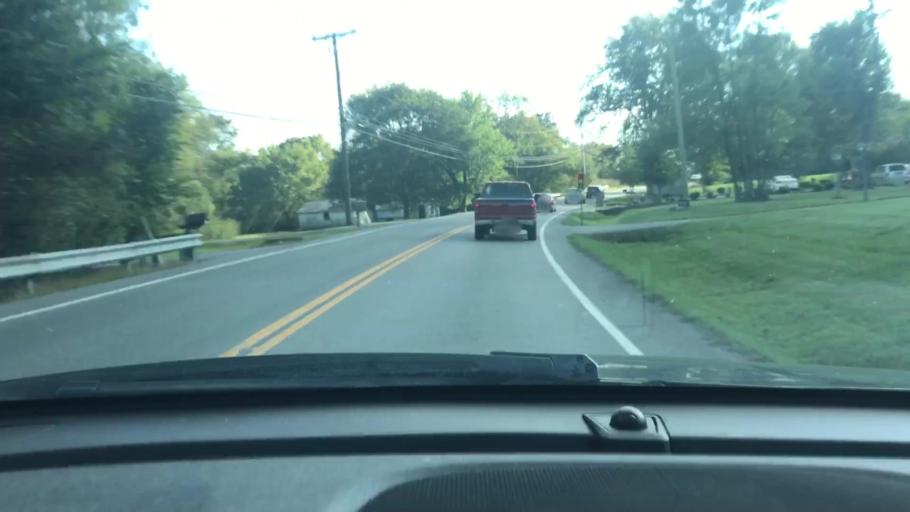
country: US
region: Tennessee
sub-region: Sumner County
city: Shackle Island
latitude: 36.3408
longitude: -86.6139
